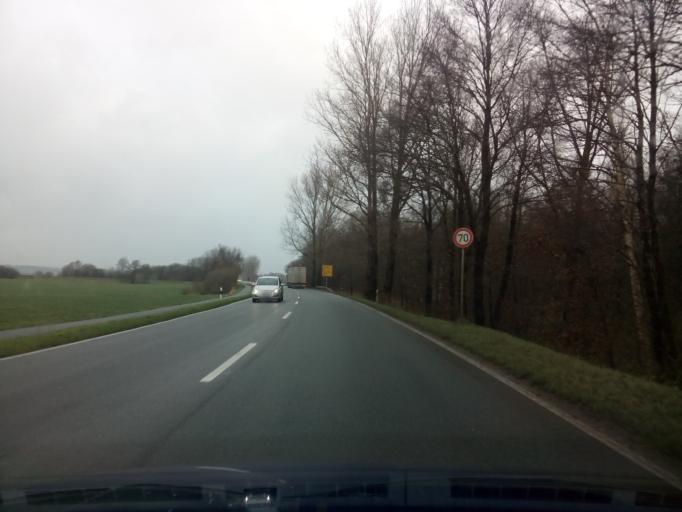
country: DE
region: Lower Saxony
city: Osterholz-Scharmbeck
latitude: 53.1910
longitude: 8.8214
